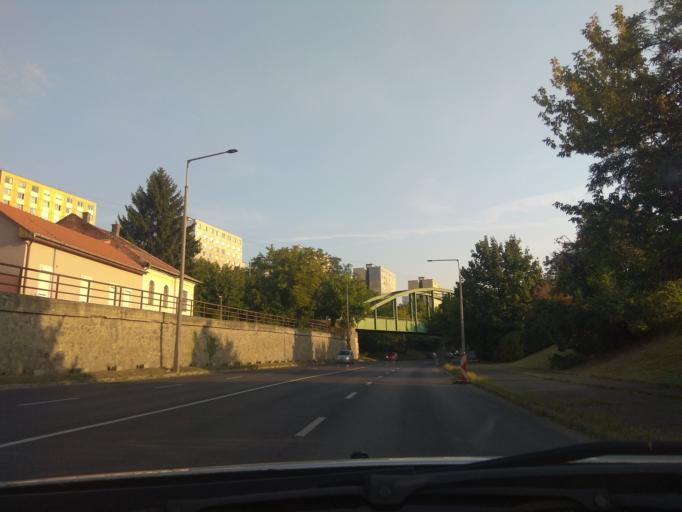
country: HU
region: Borsod-Abauj-Zemplen
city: Miskolc
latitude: 48.0771
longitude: 20.7847
